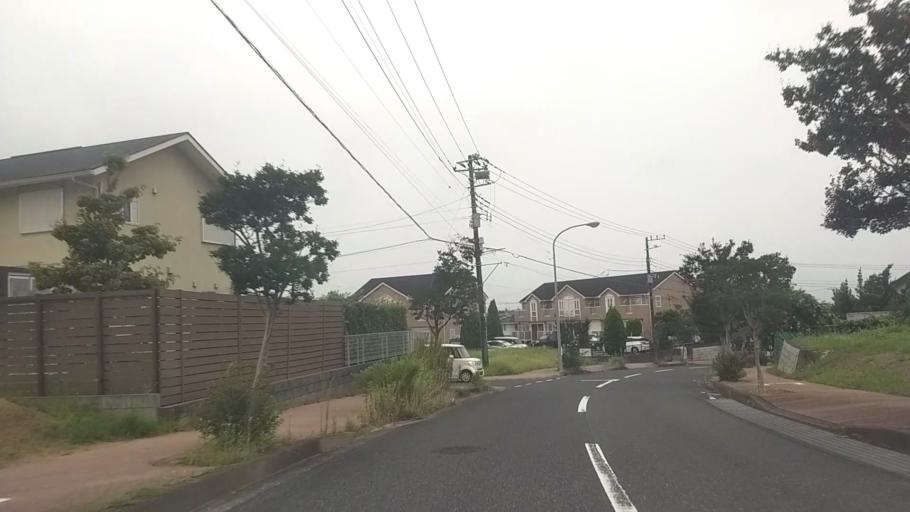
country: JP
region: Chiba
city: Kisarazu
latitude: 35.3817
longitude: 139.9654
